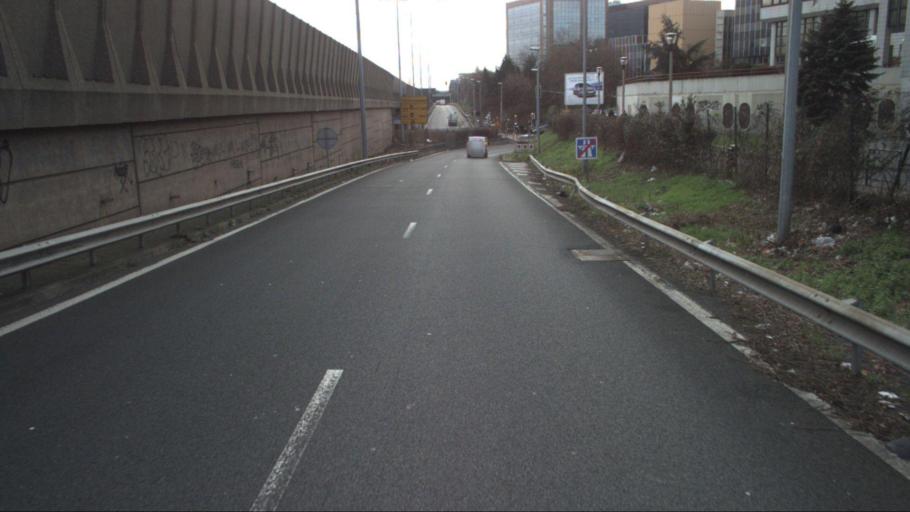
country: FR
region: Ile-de-France
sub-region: Departement du Val-de-Marne
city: Fontenay-sous-Bois
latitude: 48.8535
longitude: 2.4889
